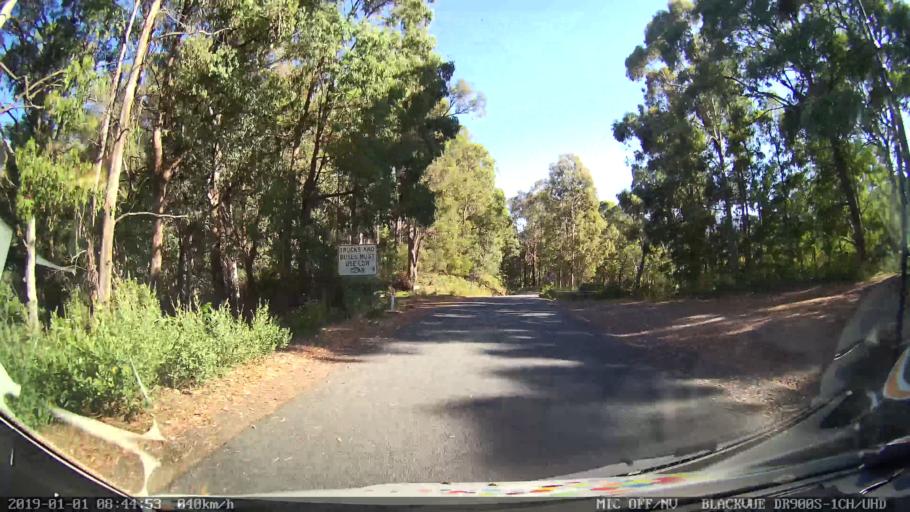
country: AU
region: New South Wales
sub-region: Snowy River
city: Jindabyne
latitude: -36.3089
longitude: 148.1878
